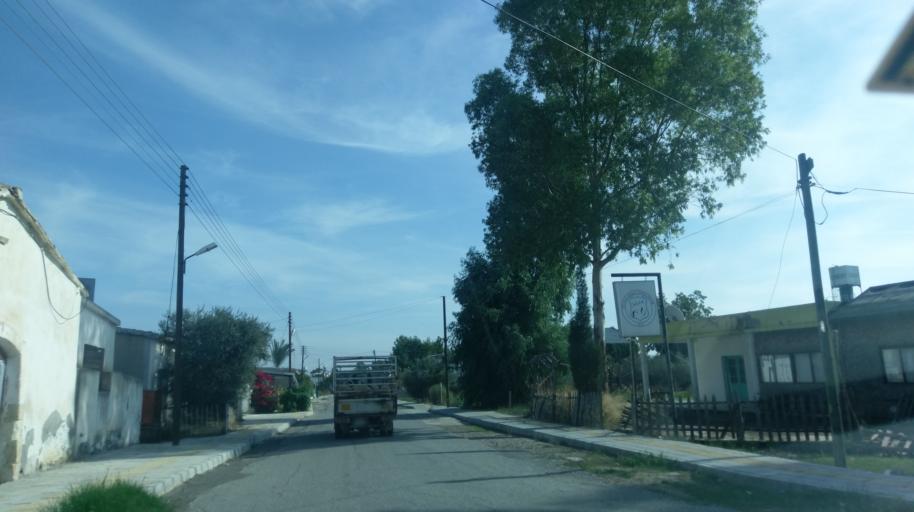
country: CY
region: Ammochostos
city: Lefkonoiko
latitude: 35.2552
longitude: 33.6861
